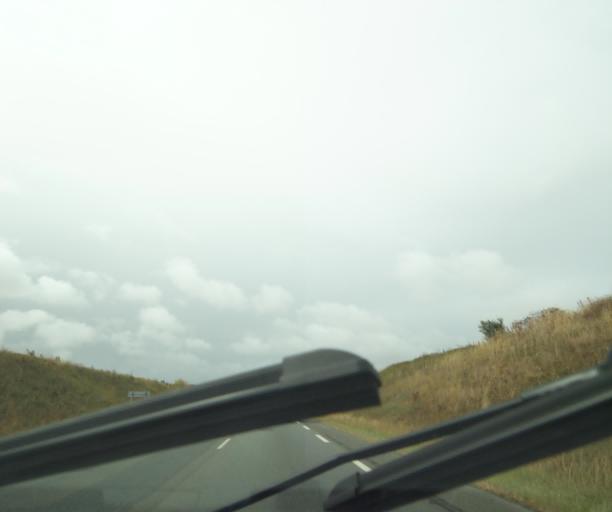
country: FR
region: Poitou-Charentes
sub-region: Departement de la Charente-Maritime
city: Lagord
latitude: 46.2006
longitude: -1.1389
